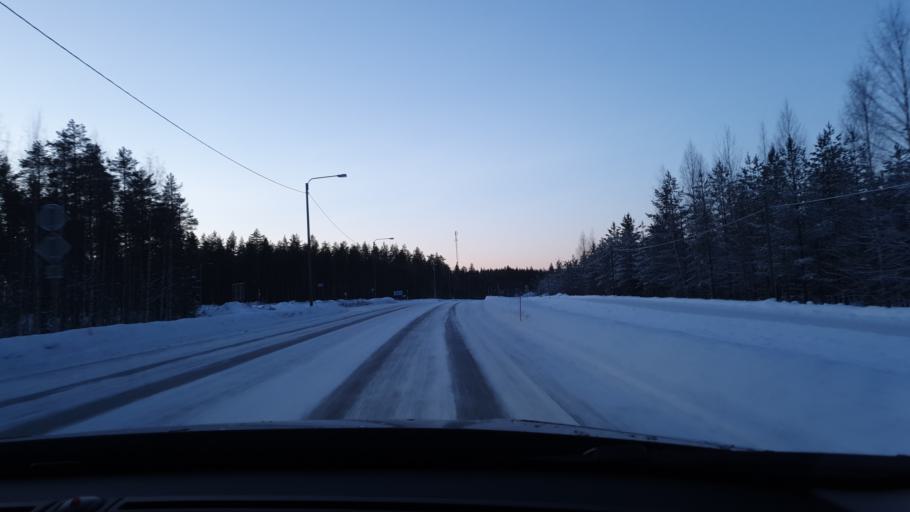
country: FI
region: Kainuu
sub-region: Kehys-Kainuu
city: Kuhmo
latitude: 64.1007
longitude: 29.4747
